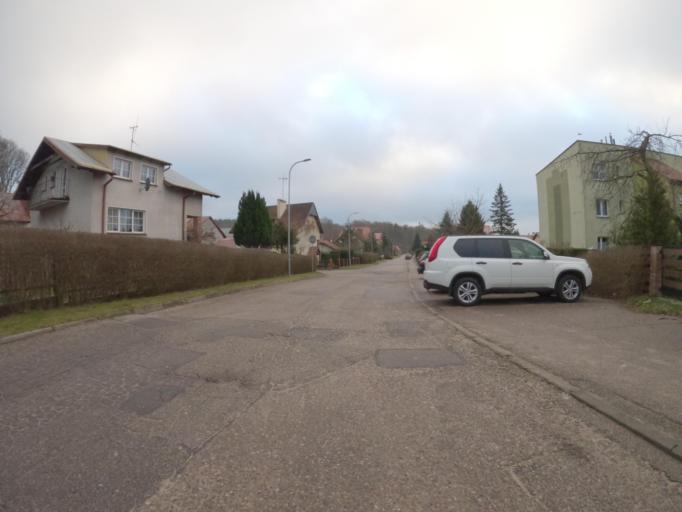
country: PL
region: West Pomeranian Voivodeship
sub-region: Koszalin
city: Koszalin
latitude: 54.2124
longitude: 16.2106
